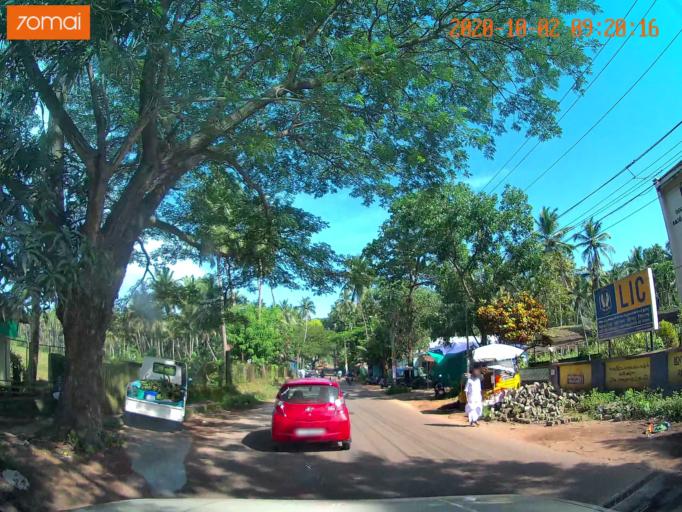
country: IN
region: Kerala
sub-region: Kozhikode
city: Naduvannur
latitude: 11.5669
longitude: 75.7550
